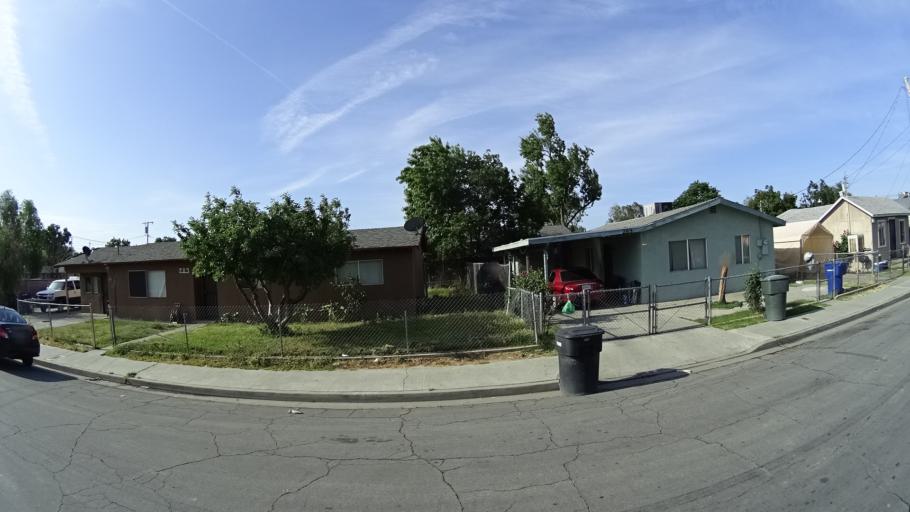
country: US
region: California
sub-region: Kings County
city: Hanford
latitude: 36.3162
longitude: -119.6478
